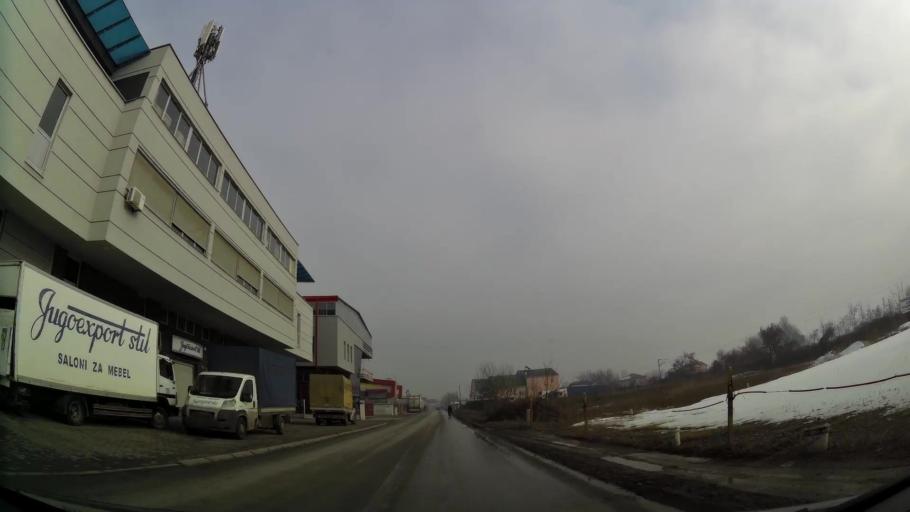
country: MK
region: Ilinden
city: Jurumleri
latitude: 41.9949
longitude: 21.5517
